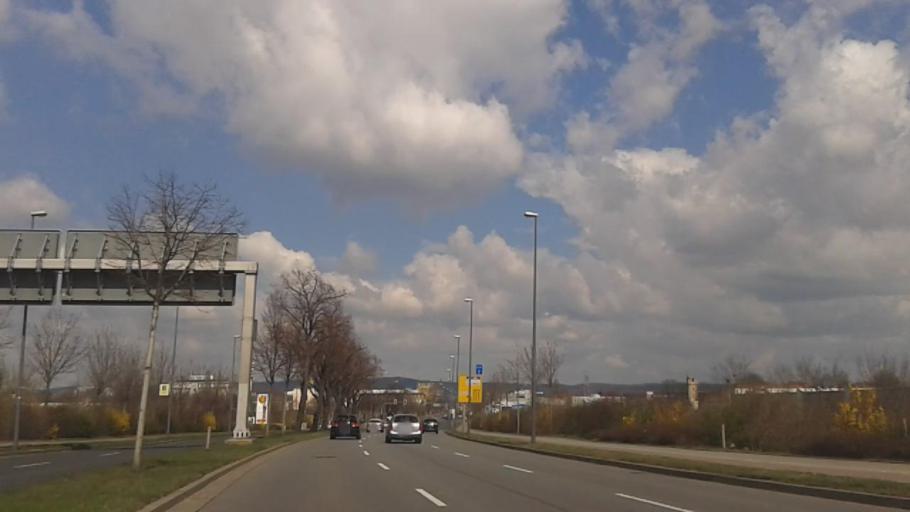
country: DE
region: Saxony
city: Radebeul
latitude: 51.0660
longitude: 13.6895
